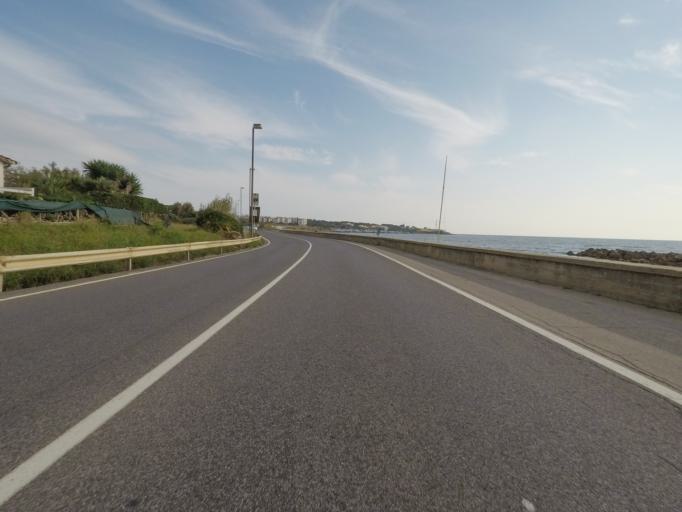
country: IT
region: Latium
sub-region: Citta metropolitana di Roma Capitale
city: Santa Marinella
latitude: 42.0401
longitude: 11.8292
